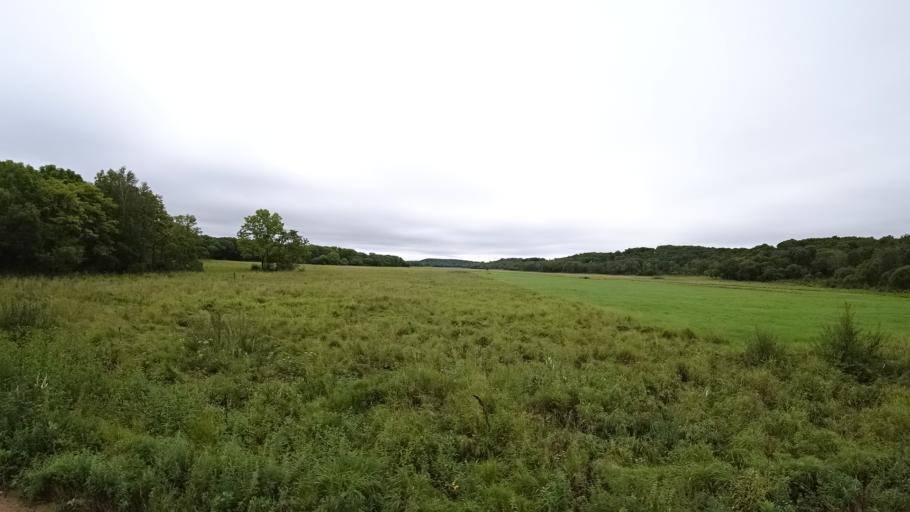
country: RU
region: Primorskiy
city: Rettikhovka
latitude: 44.0632
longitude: 132.6530
